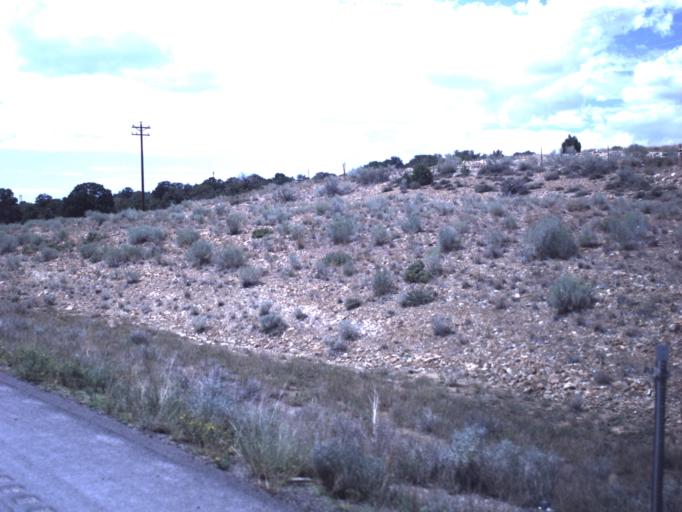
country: US
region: Utah
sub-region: Duchesne County
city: Duchesne
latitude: 40.1750
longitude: -110.5420
